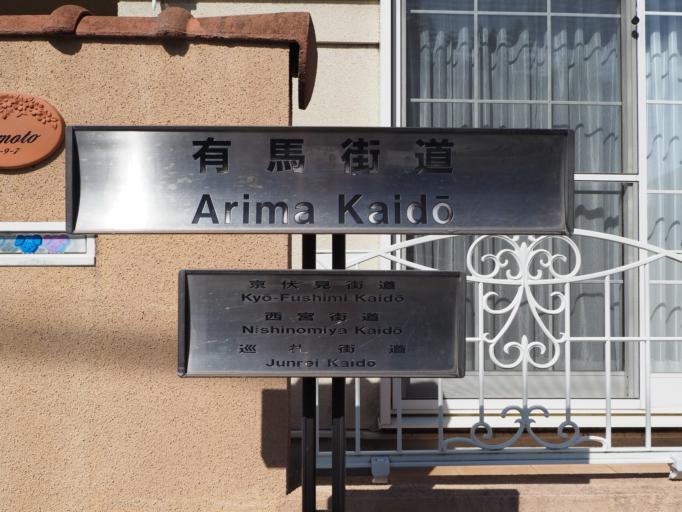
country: JP
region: Hyogo
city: Takarazuka
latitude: 34.8136
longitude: 135.3407
